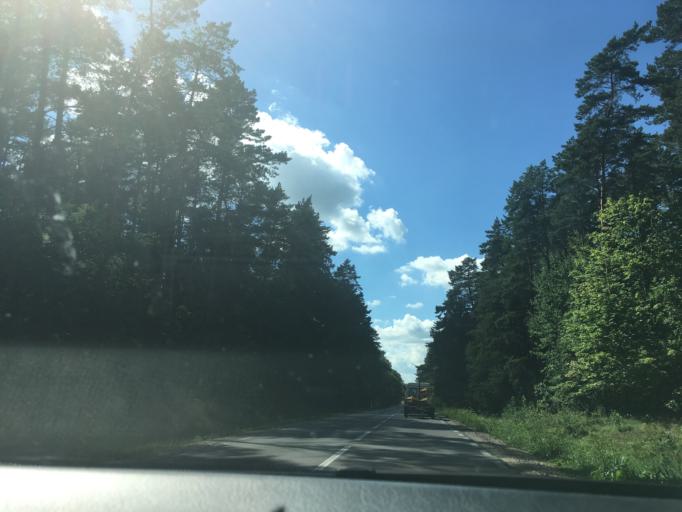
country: PL
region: Podlasie
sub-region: Powiat augustowski
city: Augustow
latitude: 53.8470
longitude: 23.0120
